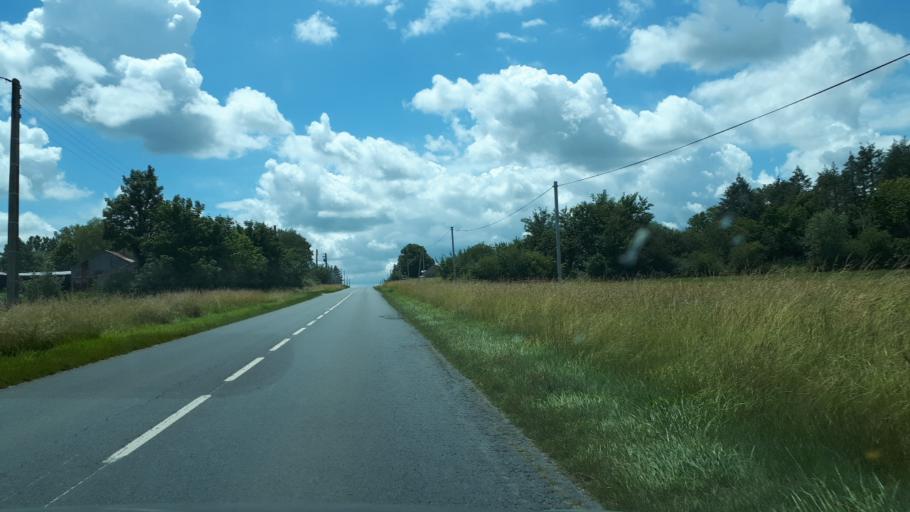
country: FR
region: Centre
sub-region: Departement du Loir-et-Cher
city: Contres
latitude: 47.4065
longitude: 1.4194
